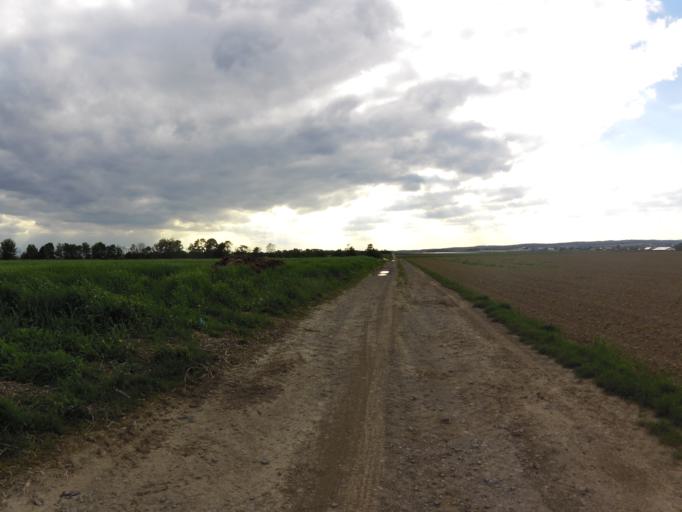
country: DE
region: Bavaria
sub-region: Regierungsbezirk Unterfranken
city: Oberpleichfeld
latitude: 49.8584
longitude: 10.0697
